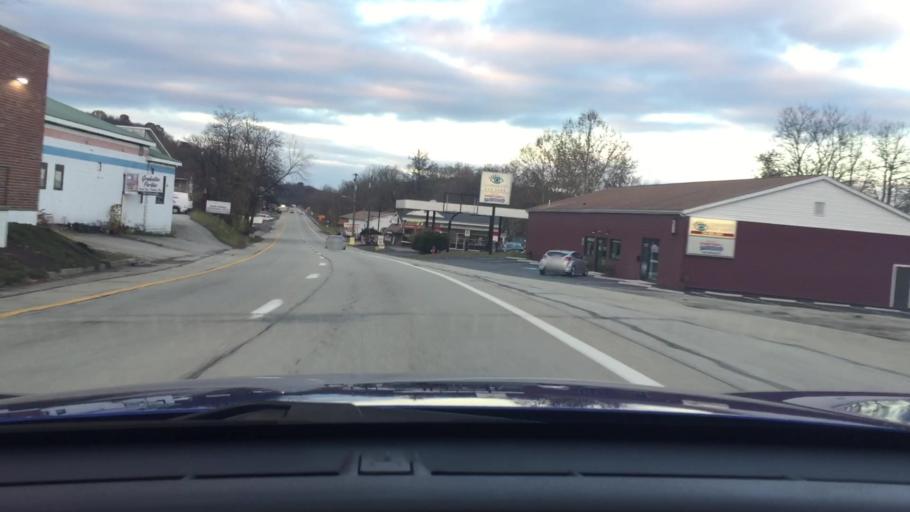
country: US
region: Pennsylvania
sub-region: Westmoreland County
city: Youngwood
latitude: 40.2430
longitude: -79.5758
